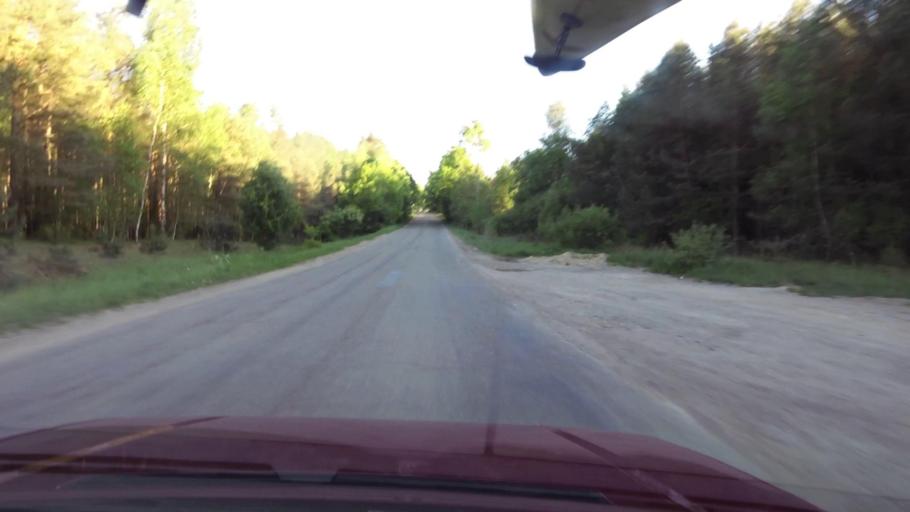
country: PL
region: West Pomeranian Voivodeship
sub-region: Powiat szczecinecki
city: Bialy Bor
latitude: 53.9162
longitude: 16.8057
